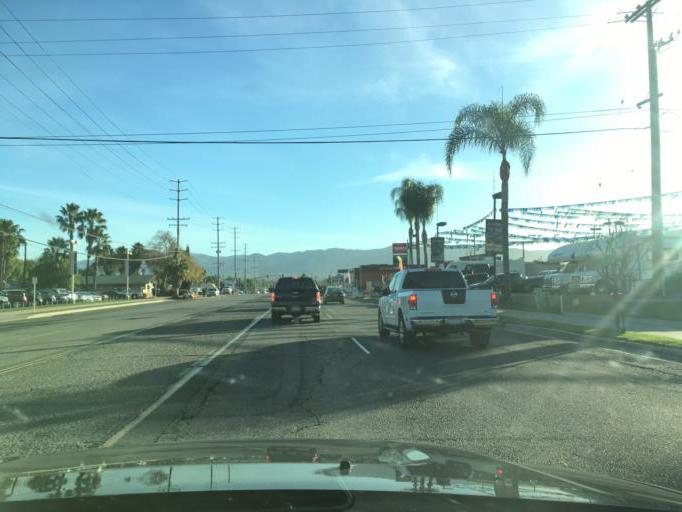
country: US
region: California
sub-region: Riverside County
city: Norco
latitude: 33.9190
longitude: -117.5597
